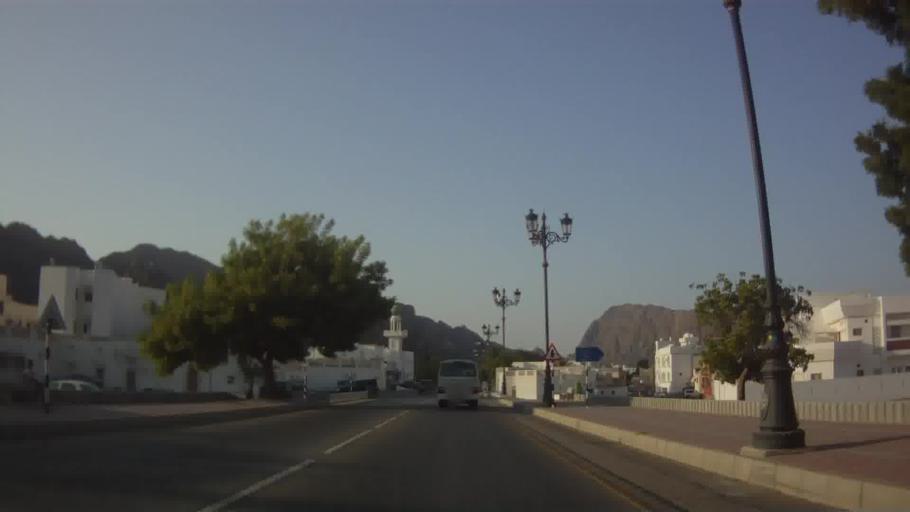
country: OM
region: Muhafazat Masqat
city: Muscat
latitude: 23.5948
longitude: 58.5978
